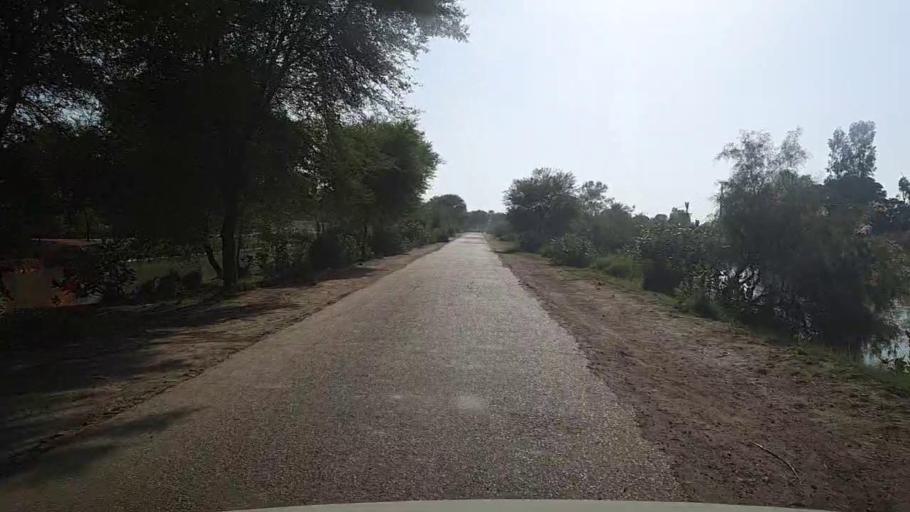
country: PK
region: Sindh
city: Kandhkot
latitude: 28.3536
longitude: 69.3731
